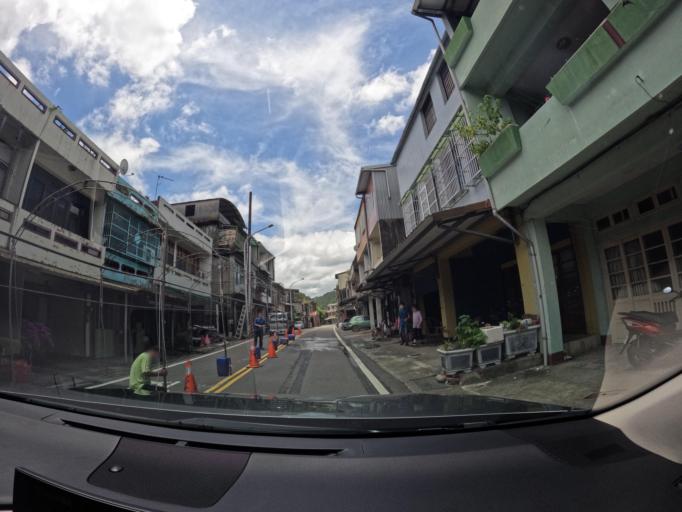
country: TW
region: Taiwan
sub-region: Hsinchu
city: Hsinchu
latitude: 24.6275
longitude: 121.0102
